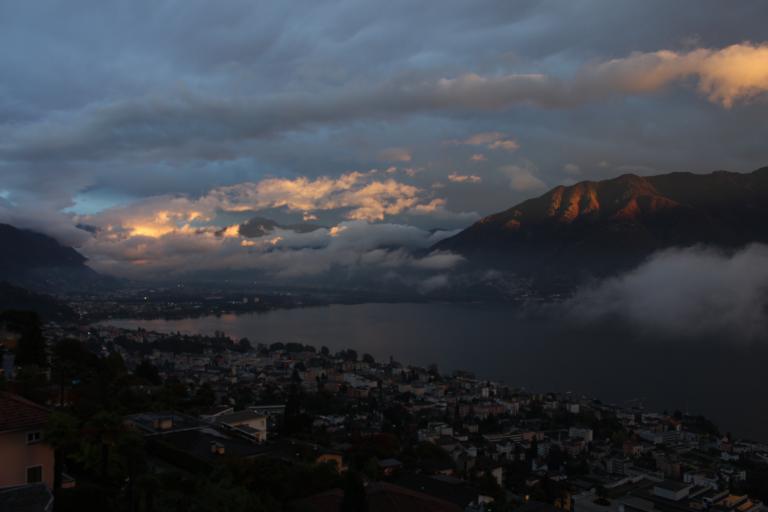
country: CH
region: Ticino
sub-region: Locarno District
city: Locarno
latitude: 46.1800
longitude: 8.8004
